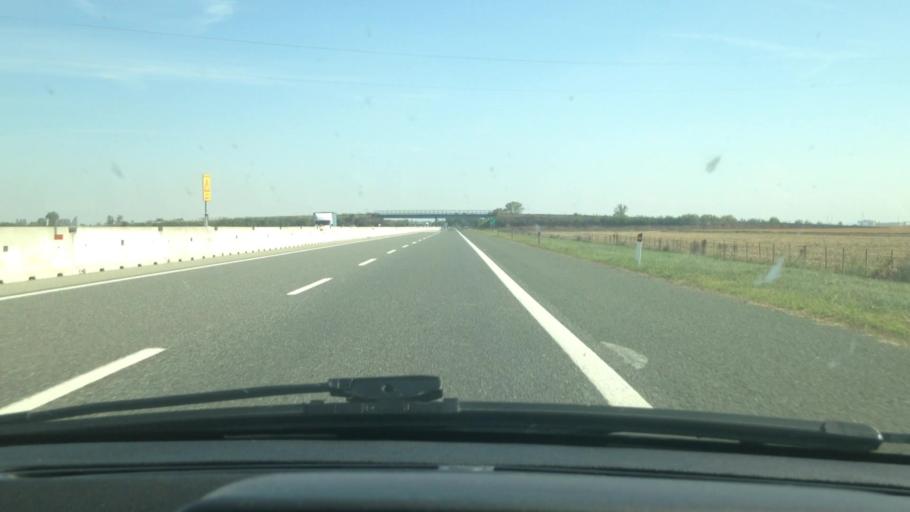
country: IT
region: Piedmont
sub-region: Provincia di Vercelli
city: Salasco
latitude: 45.3108
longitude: 8.2849
